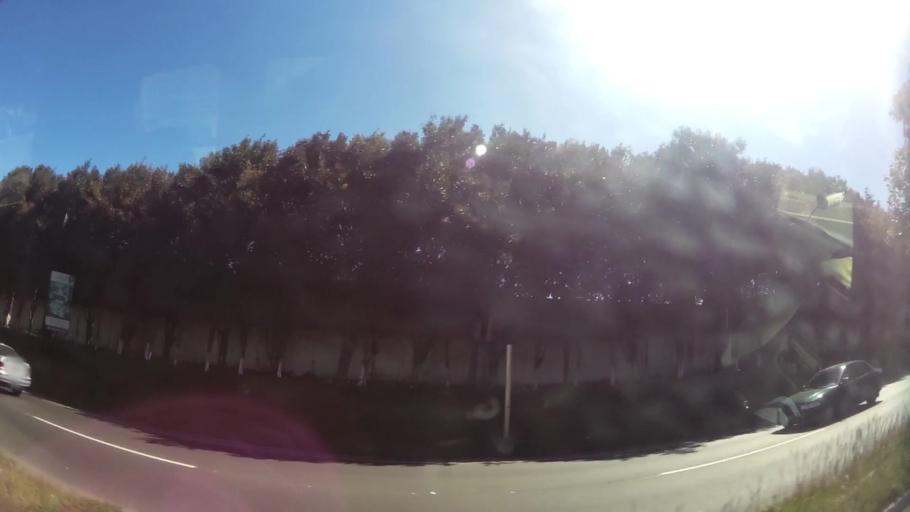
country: GT
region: Guatemala
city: Santa Catarina Pinula
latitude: 14.5303
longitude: -90.4639
